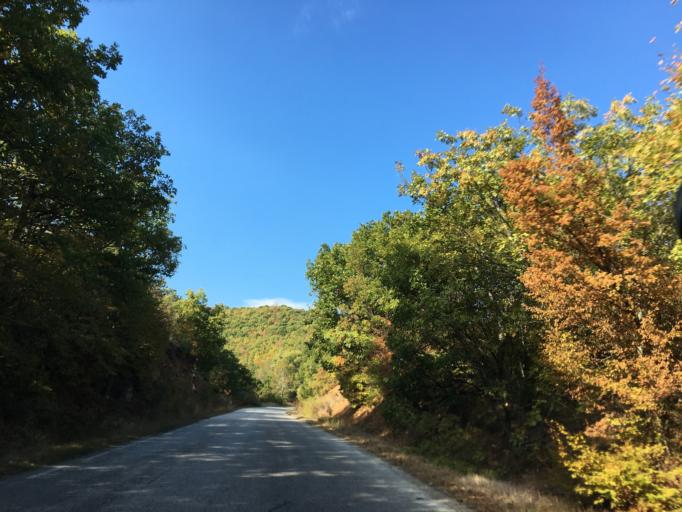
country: BG
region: Khaskovo
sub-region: Obshtina Ivaylovgrad
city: Ivaylovgrad
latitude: 41.5369
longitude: 26.0866
